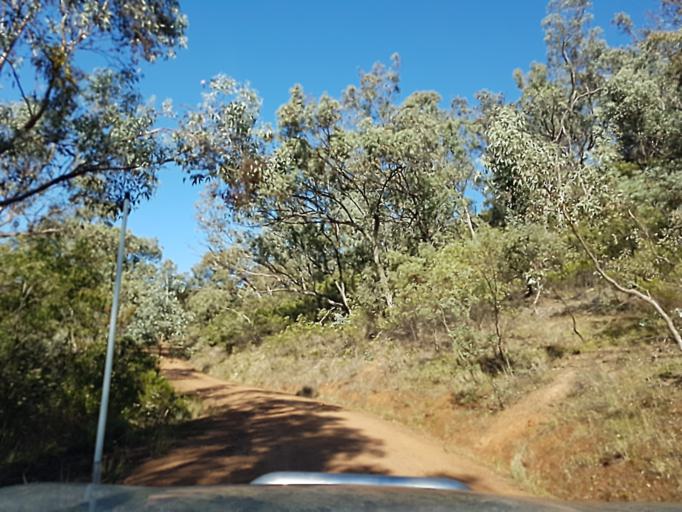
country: AU
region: New South Wales
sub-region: Snowy River
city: Jindabyne
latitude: -36.9315
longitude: 148.3345
